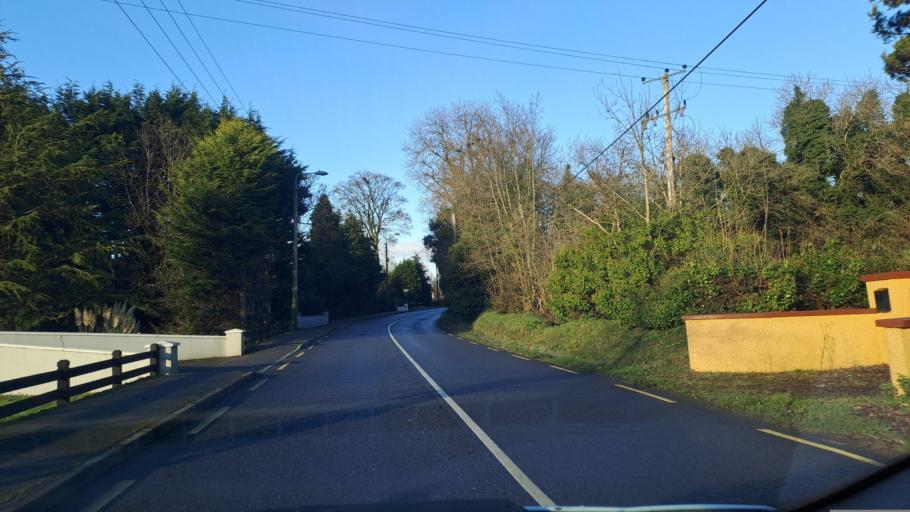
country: IE
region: Ulster
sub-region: An Cabhan
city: Bailieborough
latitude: 53.9117
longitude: -6.9697
